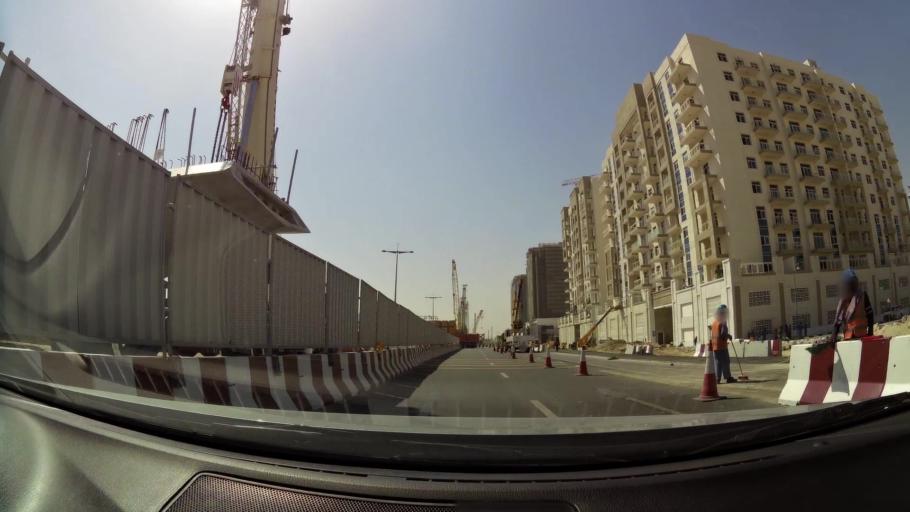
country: AE
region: Dubai
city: Dubai
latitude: 25.0273
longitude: 55.1552
